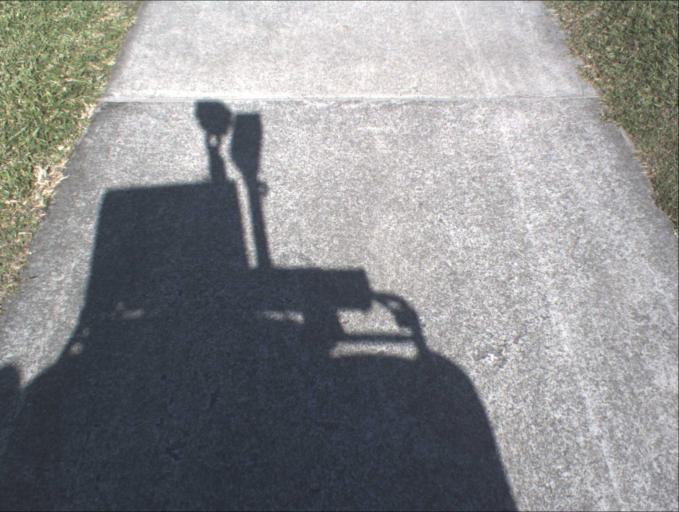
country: AU
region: Queensland
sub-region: Logan
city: North Maclean
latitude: -27.8064
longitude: 152.9593
